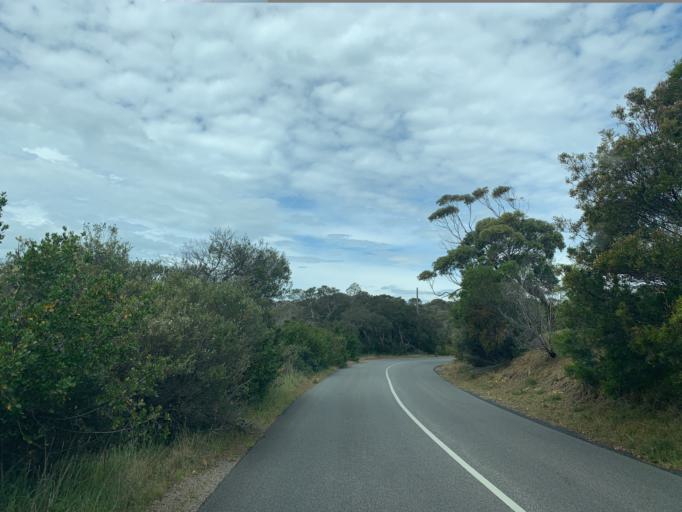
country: AU
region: Victoria
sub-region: Mornington Peninsula
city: Sorrento
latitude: -38.3176
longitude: 144.6935
